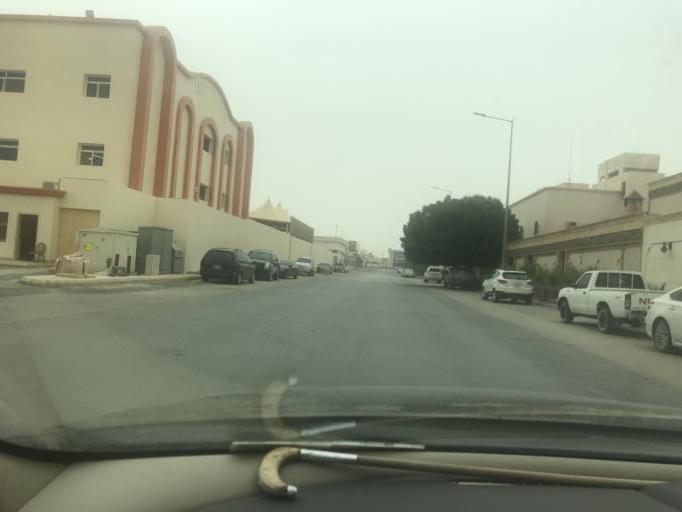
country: SA
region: Ar Riyad
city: Riyadh
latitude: 24.7270
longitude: 46.7874
